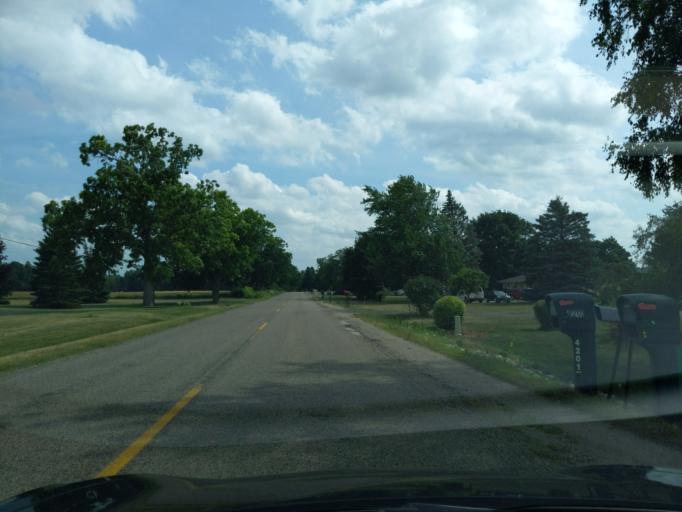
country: US
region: Michigan
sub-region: Eaton County
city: Eaton Rapids
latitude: 42.5065
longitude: -84.6307
